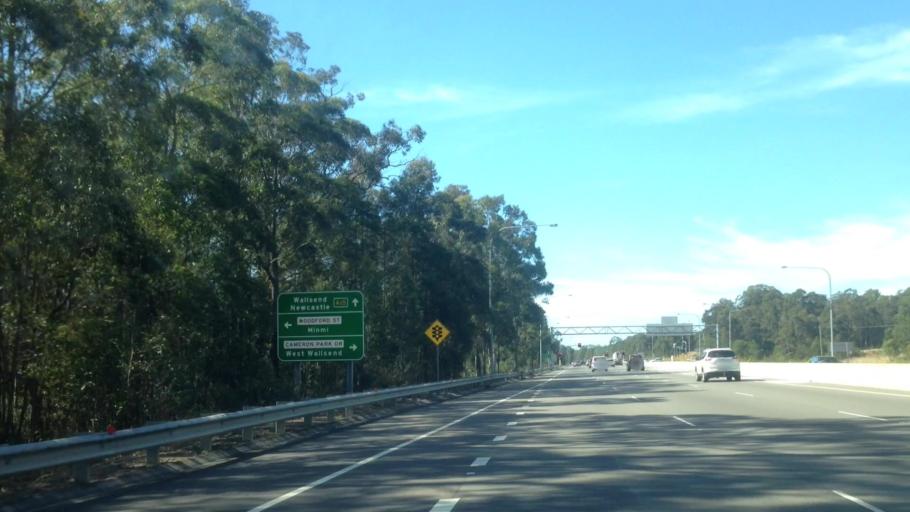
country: AU
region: New South Wales
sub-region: Lake Macquarie Shire
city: Holmesville
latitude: -32.8923
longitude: 151.6050
